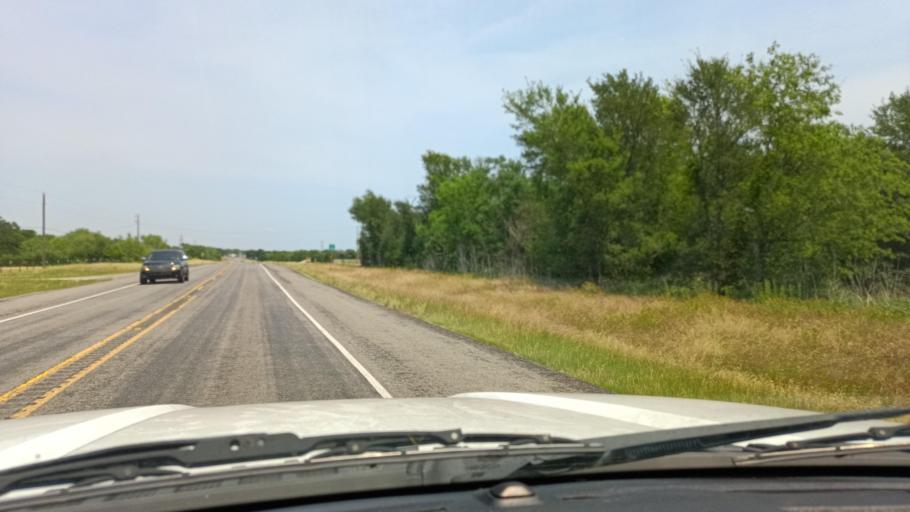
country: US
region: Texas
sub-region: Bell County
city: Rogers
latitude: 30.8767
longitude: -97.1383
